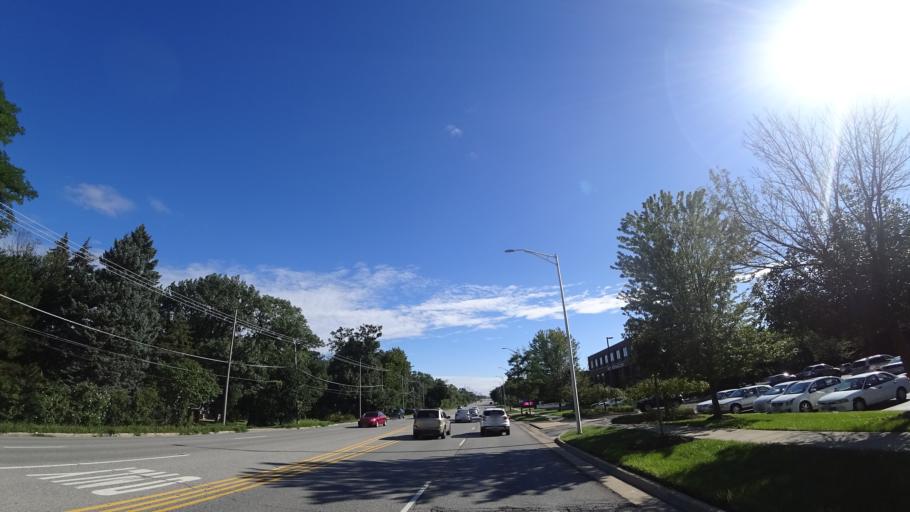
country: US
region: Illinois
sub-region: Cook County
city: Oak Forest
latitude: 41.6213
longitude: -87.7372
